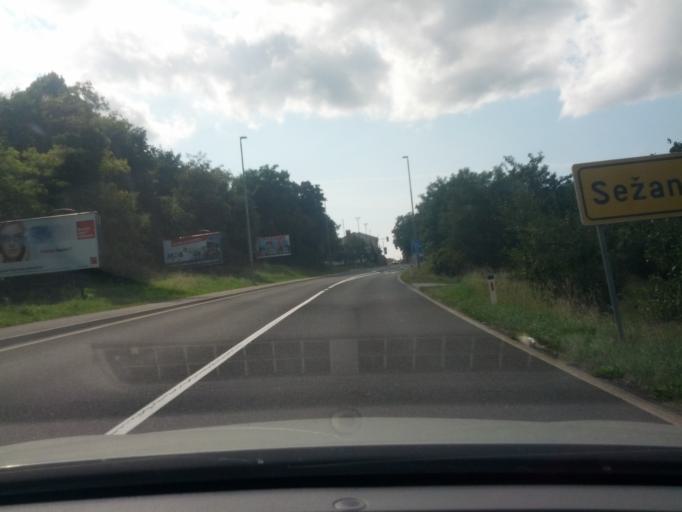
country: SI
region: Sezana
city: Sezana
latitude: 45.7111
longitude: 13.8789
